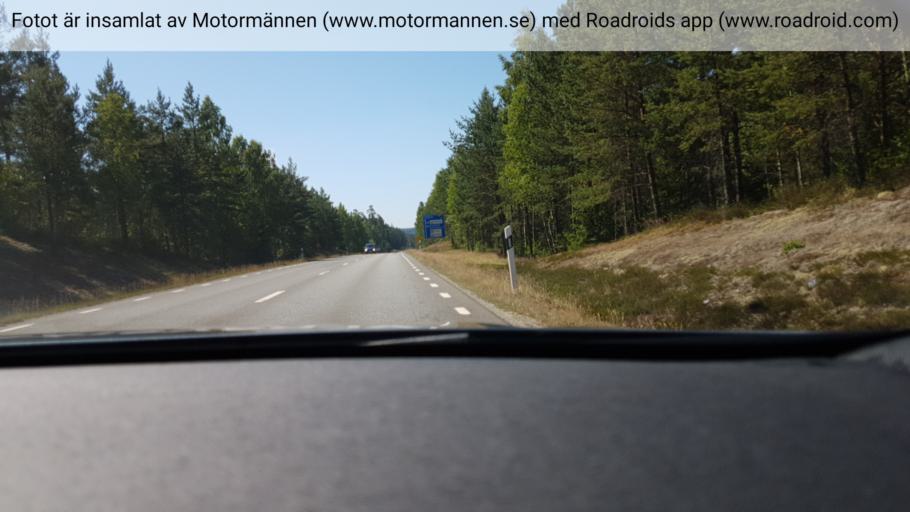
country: SE
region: Joenkoeping
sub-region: Mullsjo Kommun
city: Mullsjoe
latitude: 57.7744
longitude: 13.8347
